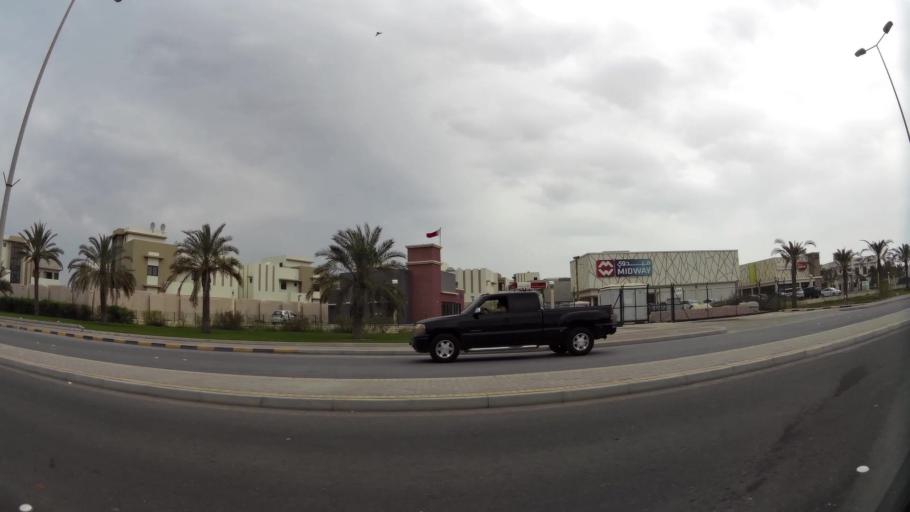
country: BH
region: Central Governorate
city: Dar Kulayb
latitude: 26.0535
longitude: 50.4871
